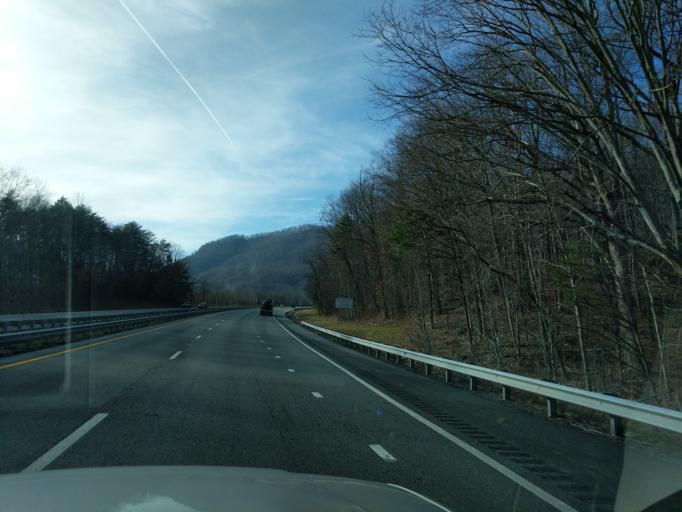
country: US
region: North Carolina
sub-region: Polk County
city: Columbus
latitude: 35.2539
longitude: -82.2329
